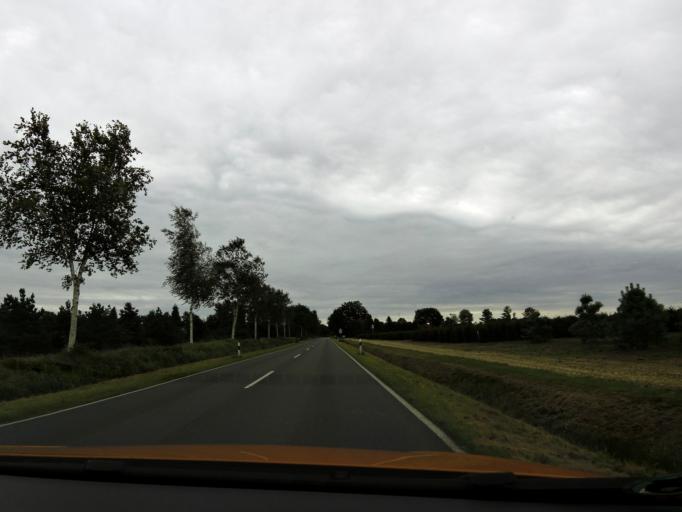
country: DE
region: Lower Saxony
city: Westerstede
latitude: 53.2502
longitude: 7.9725
